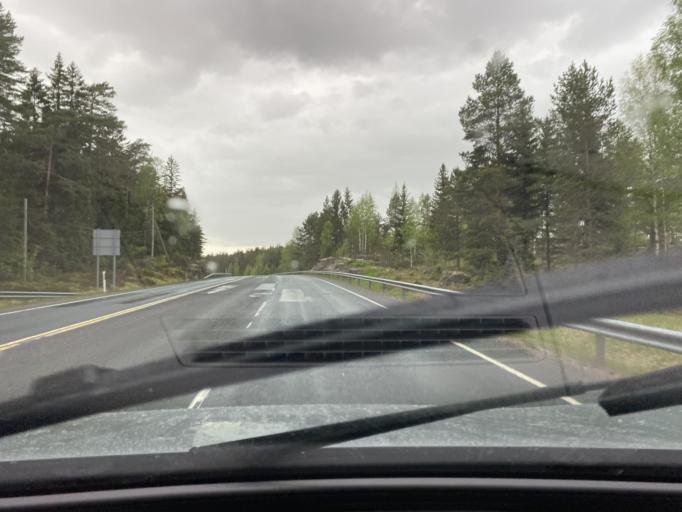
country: FI
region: Varsinais-Suomi
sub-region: Salo
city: Suomusjaervi
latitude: 60.3713
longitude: 23.6700
